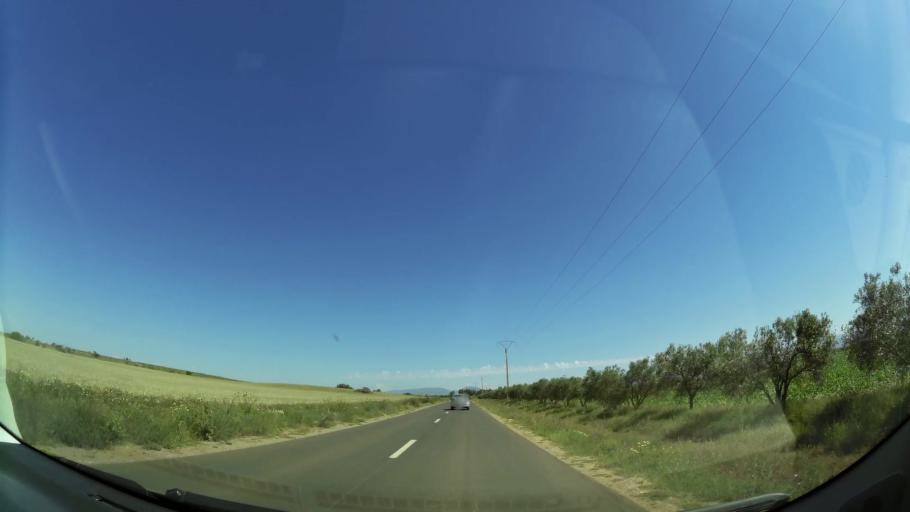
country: MA
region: Oriental
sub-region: Berkane-Taourirt
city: Madagh
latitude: 35.0315
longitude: -2.4151
